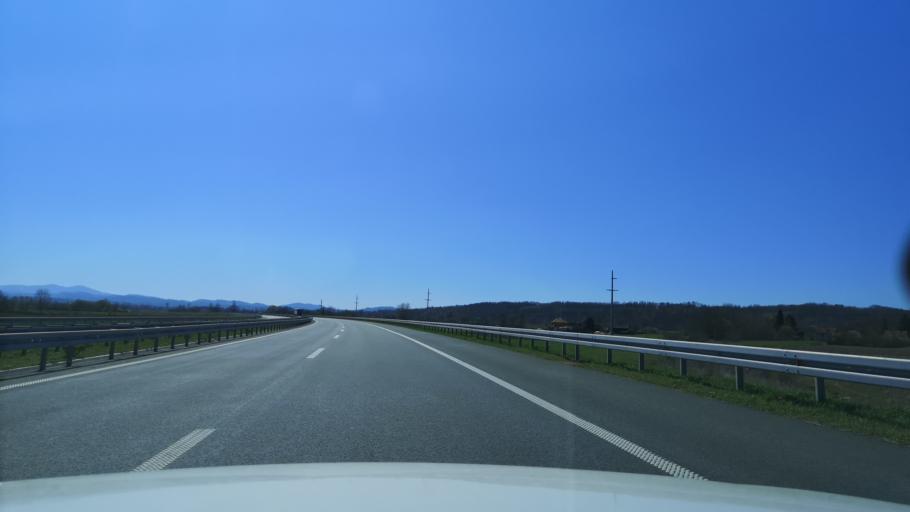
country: RS
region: Central Serbia
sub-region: Kolubarski Okrug
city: Lajkovac
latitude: 44.3152
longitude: 20.2155
